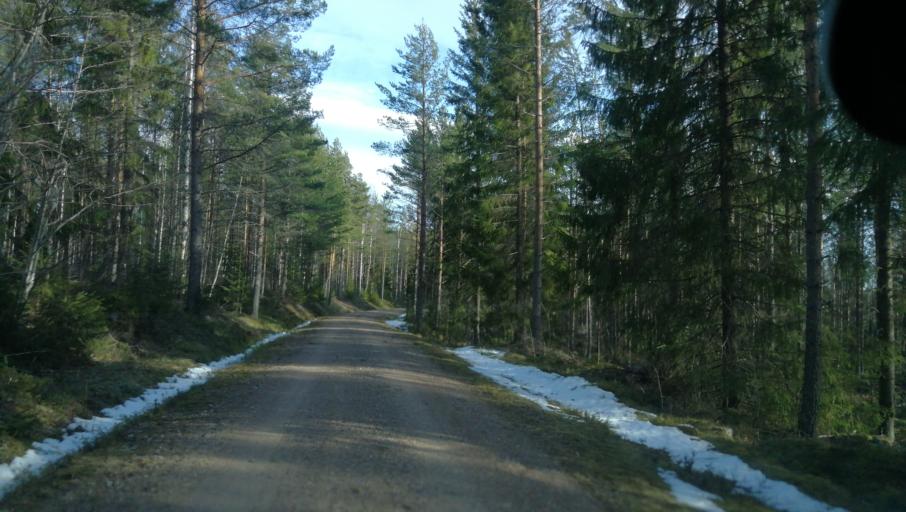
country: SE
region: Dalarna
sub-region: Vansbro Kommun
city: Vansbro
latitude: 60.7976
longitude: 14.2241
